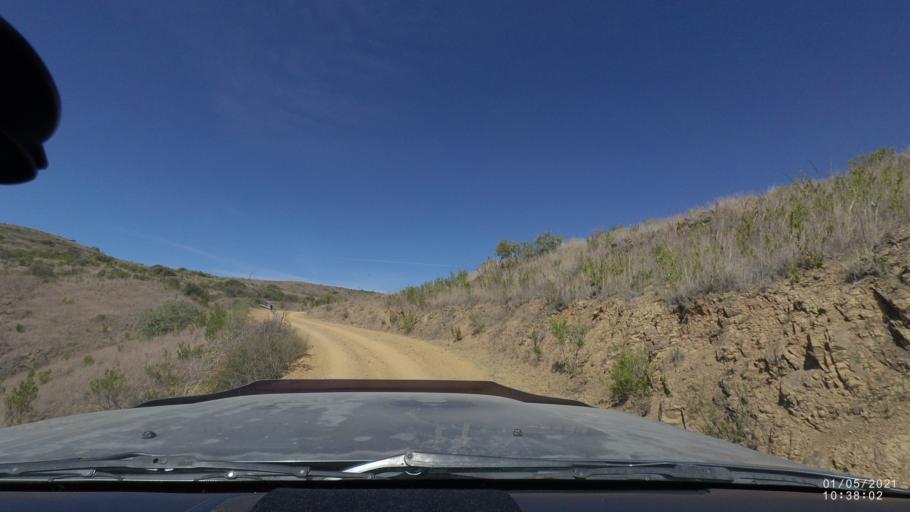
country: BO
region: Cochabamba
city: Capinota
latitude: -17.6029
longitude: -66.1852
